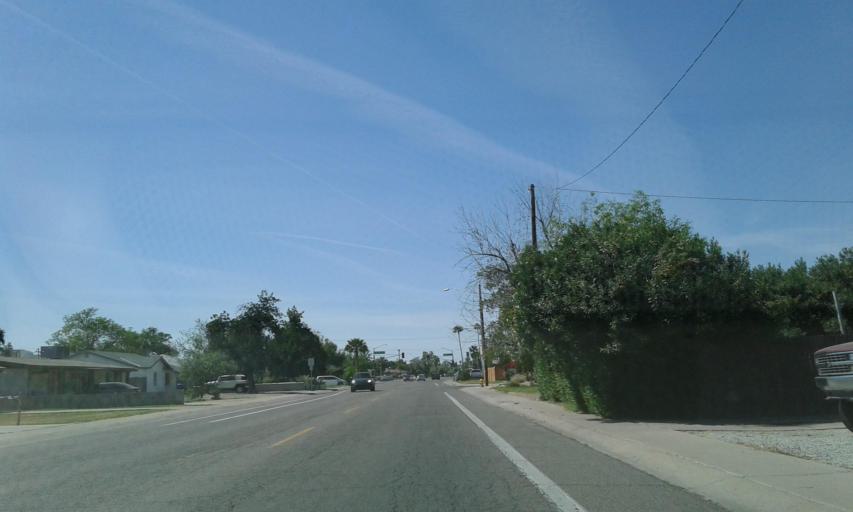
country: US
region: Arizona
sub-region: Maricopa County
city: Phoenix
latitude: 33.5023
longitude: -112.0977
